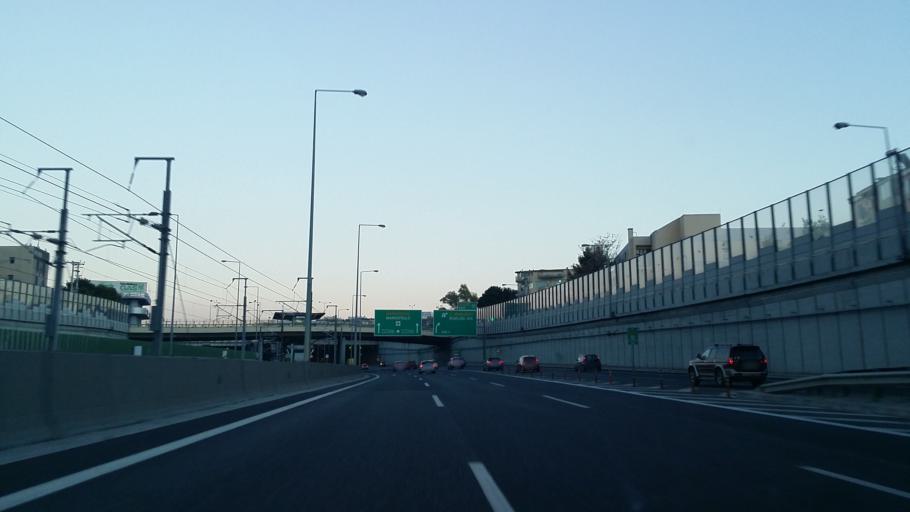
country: GR
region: Attica
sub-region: Nomarchia Athinas
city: Metamorfosi
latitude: 38.0608
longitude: 23.7529
